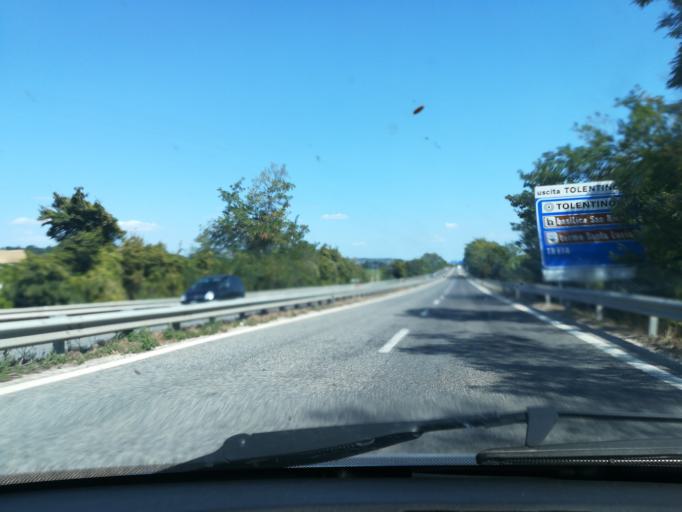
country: IT
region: The Marches
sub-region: Provincia di Macerata
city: Tolentino
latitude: 43.2073
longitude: 13.3020
